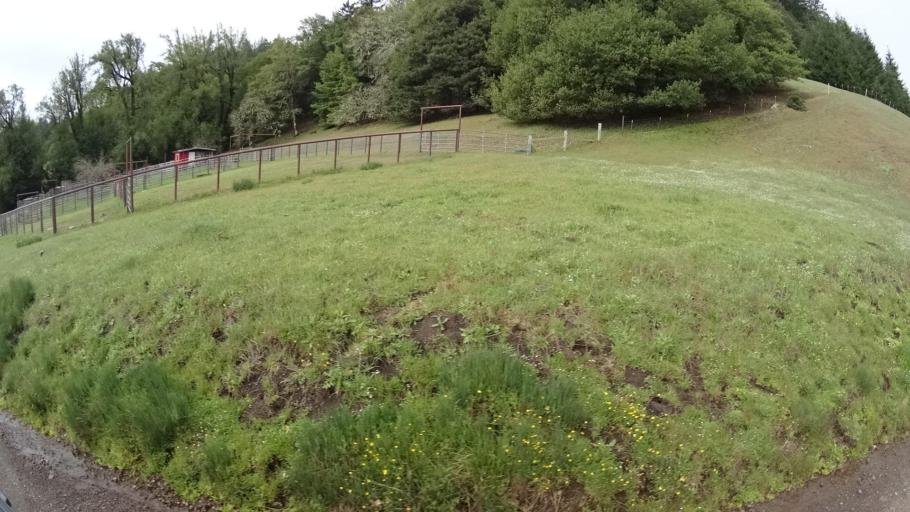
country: US
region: California
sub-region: Humboldt County
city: Redway
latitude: 40.1951
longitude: -123.7033
